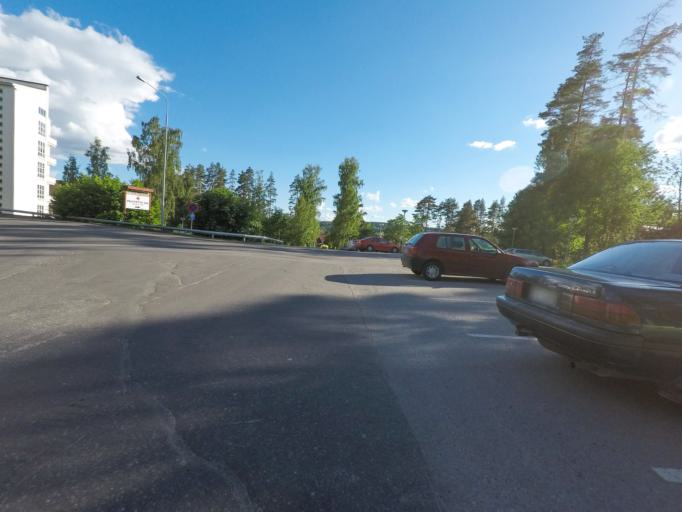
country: FI
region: Southern Savonia
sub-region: Savonlinna
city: Savonlinna
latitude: 61.8723
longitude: 28.8505
